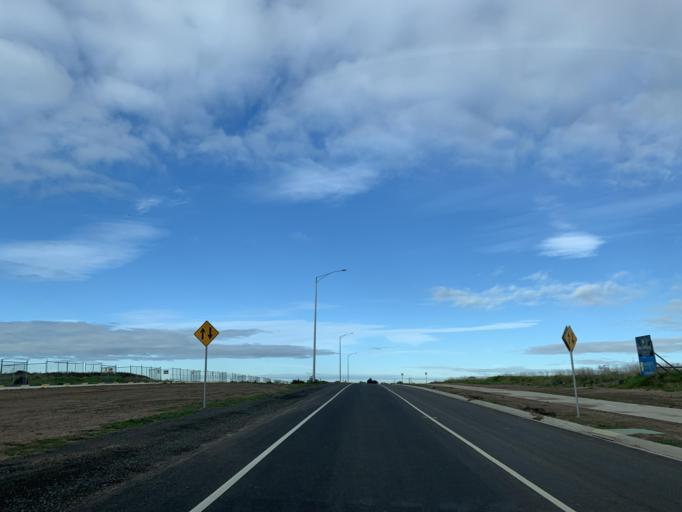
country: AU
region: Victoria
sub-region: Cardinia
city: Officer South
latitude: -38.1254
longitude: 145.3644
